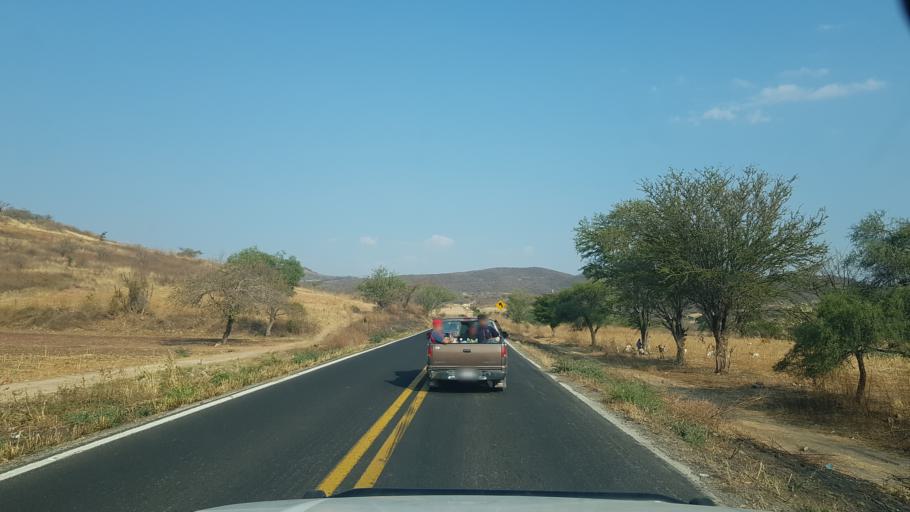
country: MX
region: Puebla
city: Calmeca
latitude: 18.6423
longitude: -98.6206
